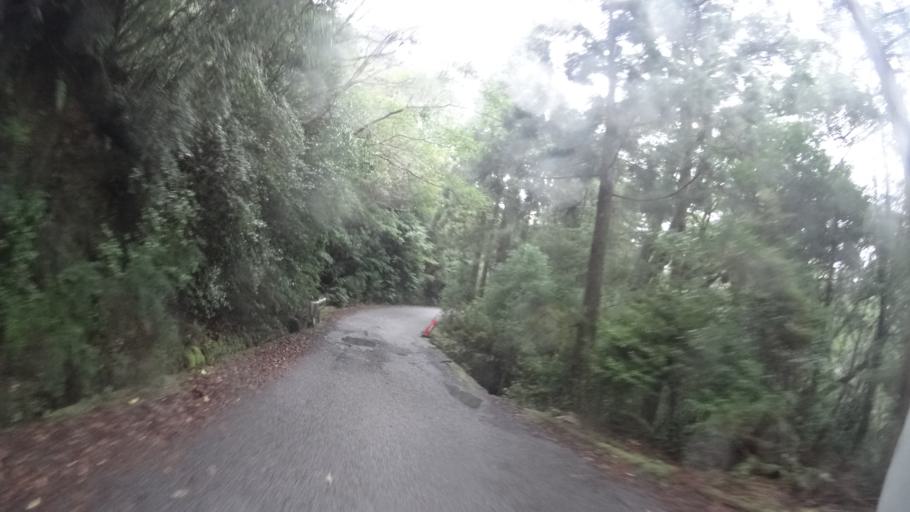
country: JP
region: Kagoshima
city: Nishinoomote
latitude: 30.3017
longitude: 130.5793
